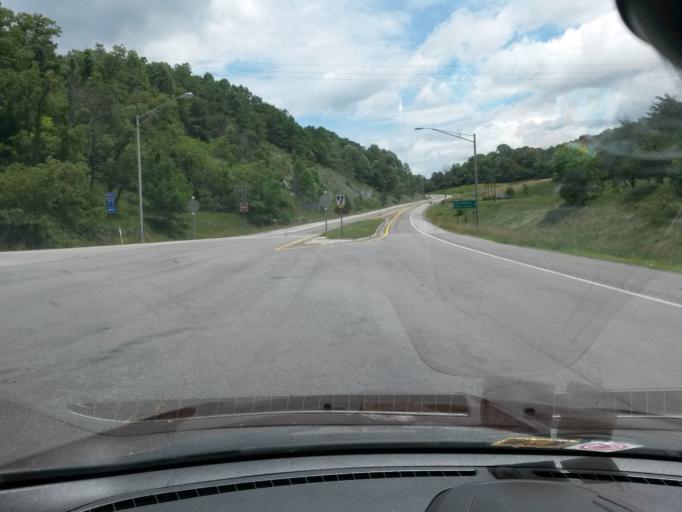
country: US
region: West Virginia
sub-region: Mercer County
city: Princeton
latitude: 37.2851
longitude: -81.1237
